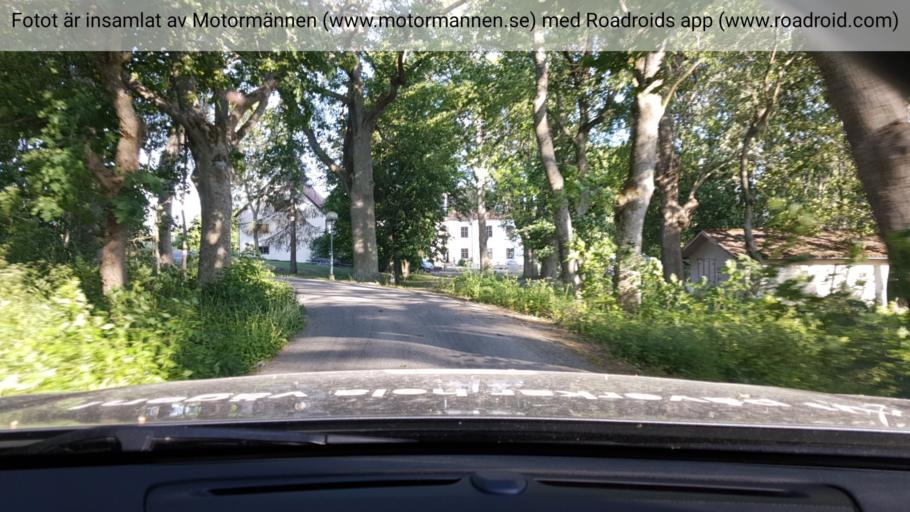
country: SE
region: Stockholm
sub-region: Haninge Kommun
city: Jordbro
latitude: 59.0084
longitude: 18.1210
